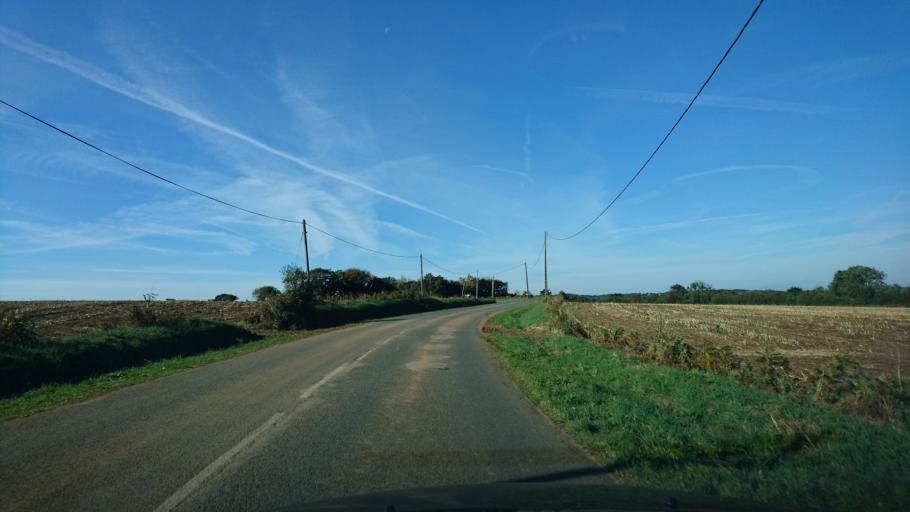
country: FR
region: Brittany
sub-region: Departement du Finistere
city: Saint-Renan
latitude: 48.4300
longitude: -4.6345
